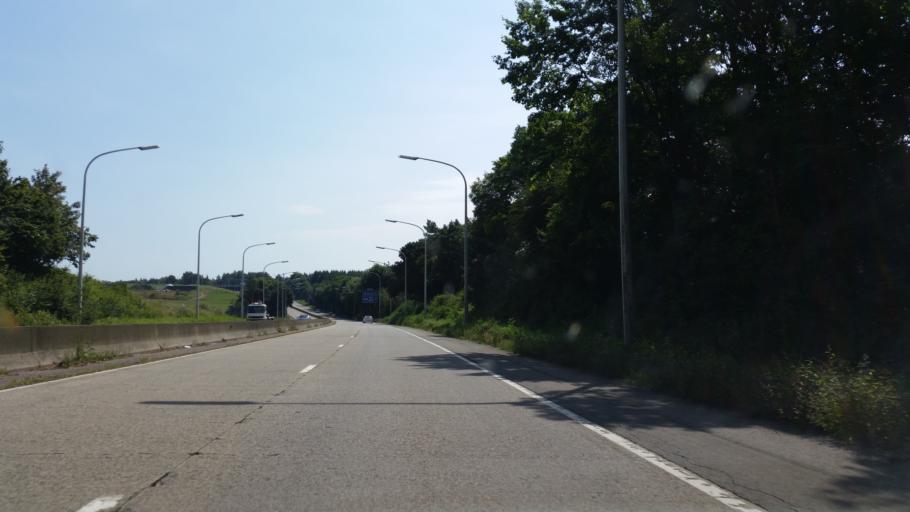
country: BE
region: Wallonia
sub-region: Province de Namur
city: Hamois
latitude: 50.2907
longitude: 5.1758
